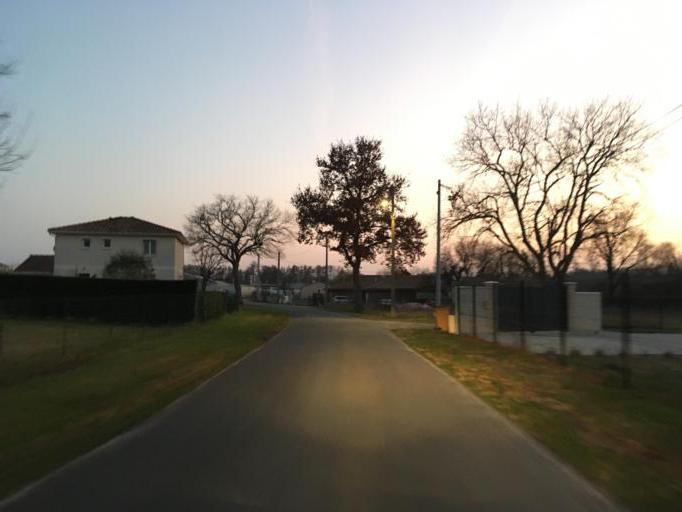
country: FR
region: Aquitaine
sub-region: Departement de la Gironde
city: Braud-et-Saint-Louis
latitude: 45.2563
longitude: -0.6240
